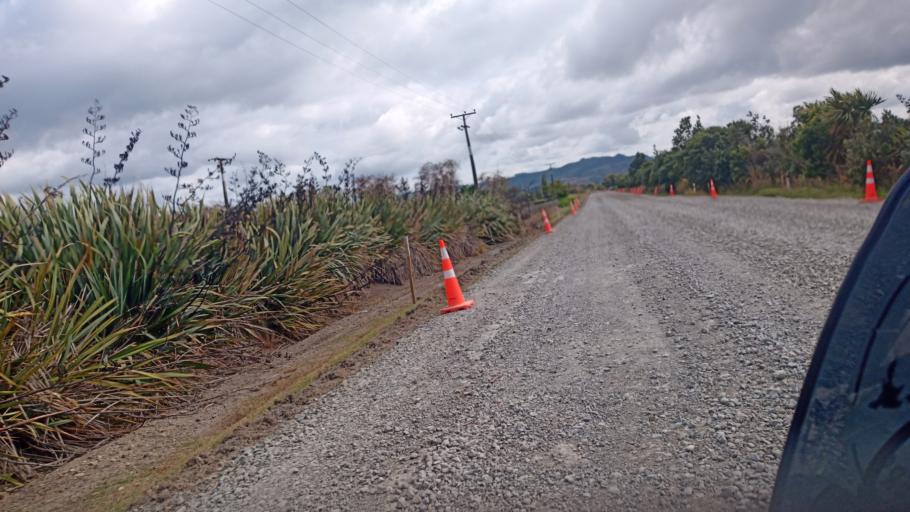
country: NZ
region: Gisborne
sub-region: Gisborne District
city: Gisborne
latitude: -38.3459
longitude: 178.2988
